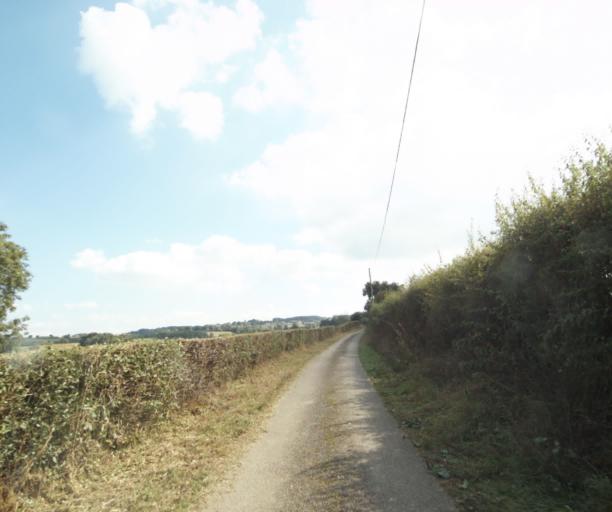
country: FR
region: Bourgogne
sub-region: Departement de Saone-et-Loire
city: Charolles
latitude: 46.3559
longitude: 4.2437
